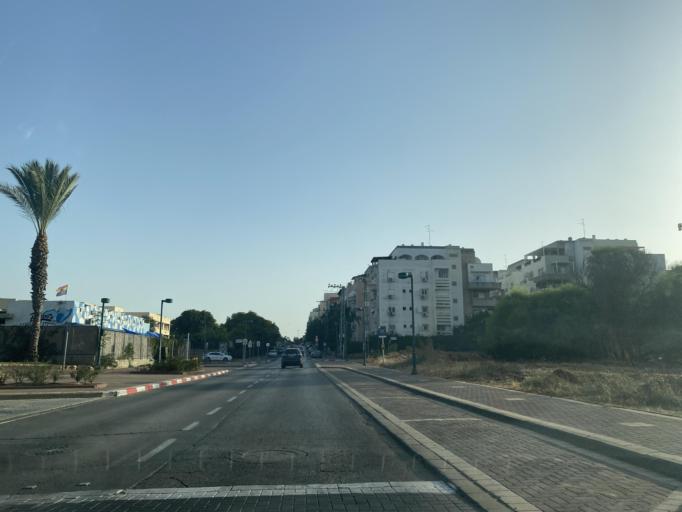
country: IL
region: Central District
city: Kfar Saba
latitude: 32.1629
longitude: 34.9073
